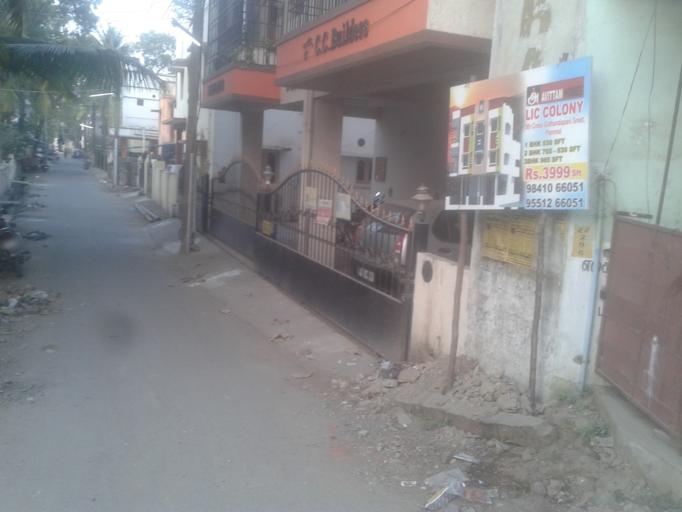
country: IN
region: Tamil Nadu
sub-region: Kancheepuram
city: Pallavaram
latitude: 12.9748
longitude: 80.1280
